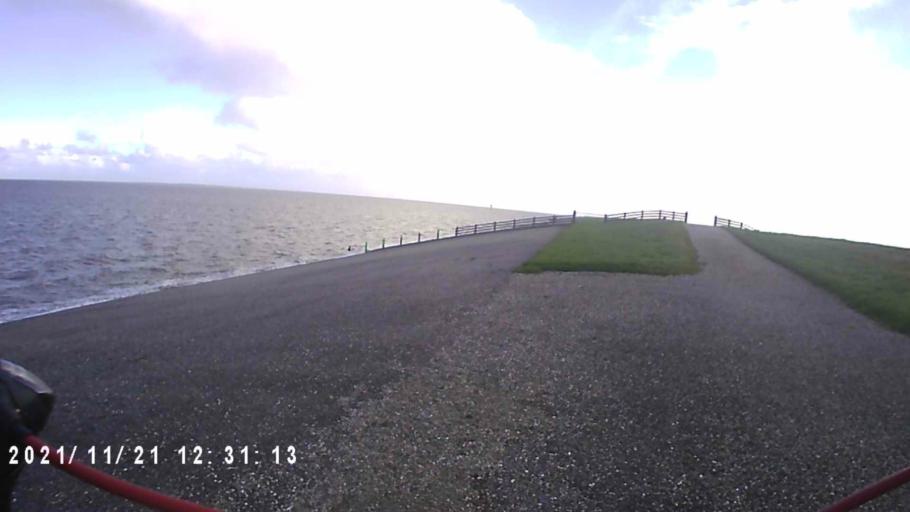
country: NL
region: Friesland
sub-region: Gemeente Dongeradeel
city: Anjum
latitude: 53.4046
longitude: 6.0487
